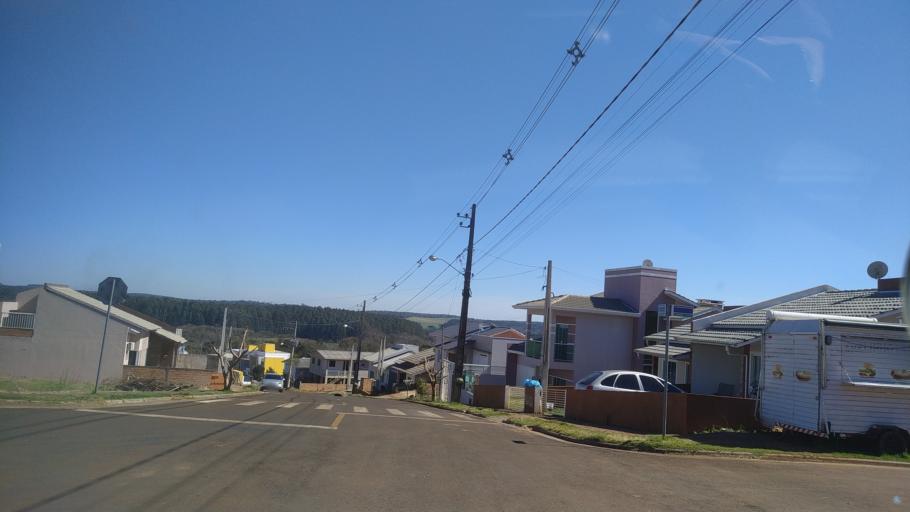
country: BR
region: Santa Catarina
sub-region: Chapeco
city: Chapeco
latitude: -27.0881
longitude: -52.7131
